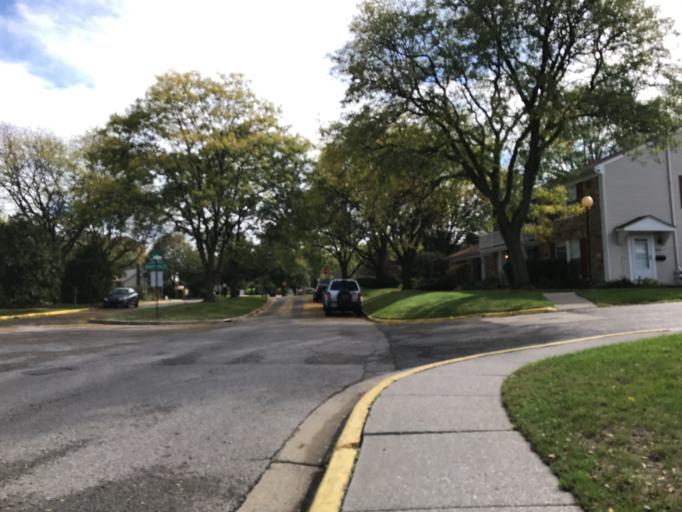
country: US
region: Michigan
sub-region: Washtenaw County
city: Ann Arbor
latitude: 42.2455
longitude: -83.7280
